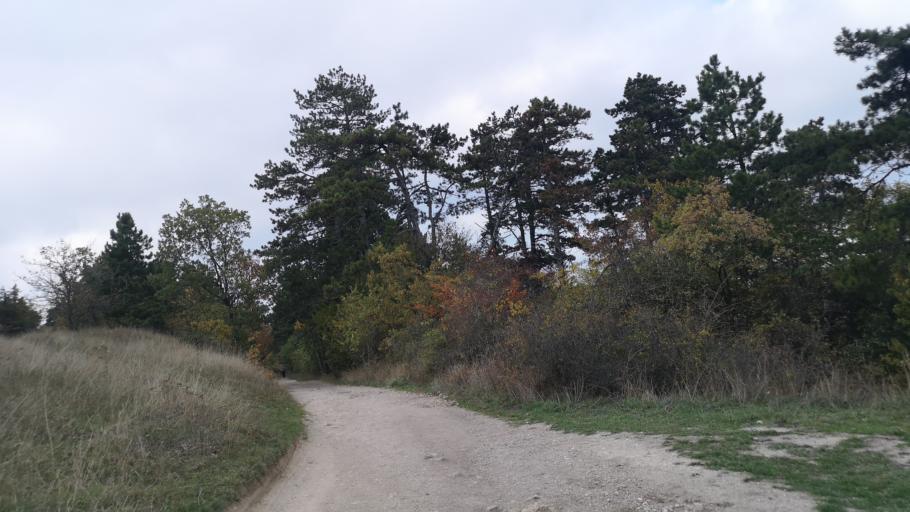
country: SK
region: Nitriansky
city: Cachtice
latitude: 48.7223
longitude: 17.7634
